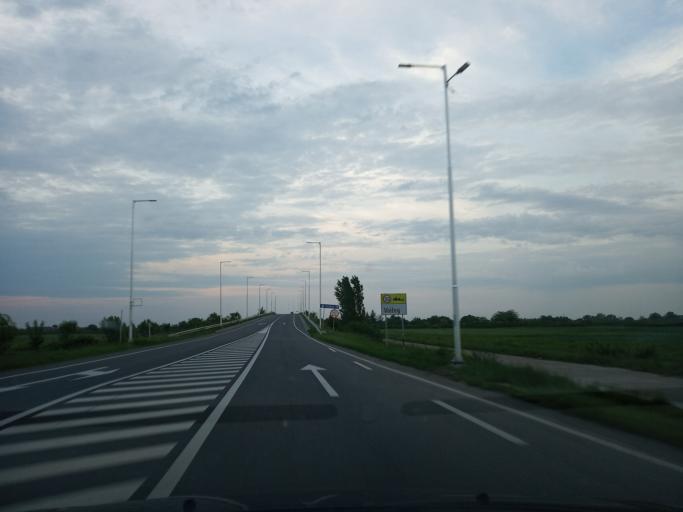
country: RO
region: Timis
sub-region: Comuna Voiteg
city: Voiteg
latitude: 45.4609
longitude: 21.2352
